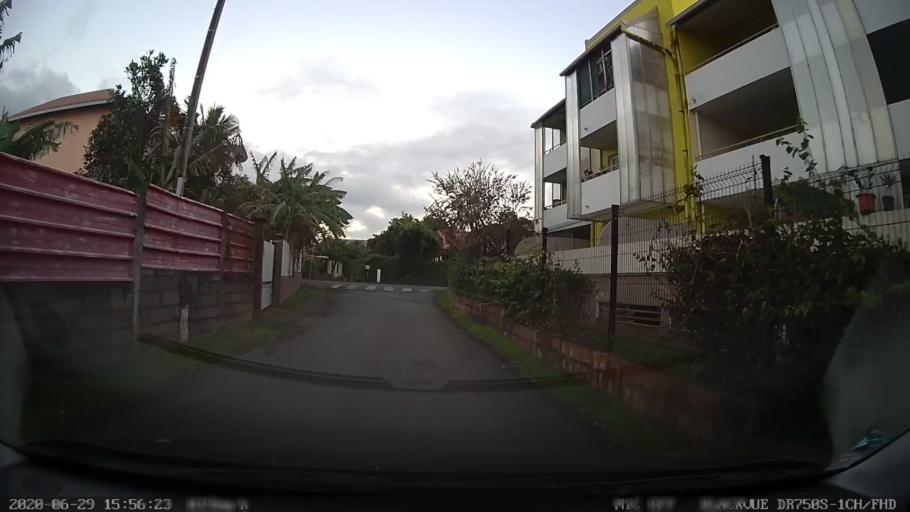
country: RE
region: Reunion
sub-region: Reunion
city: Bras-Panon
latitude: -20.9994
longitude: 55.6942
